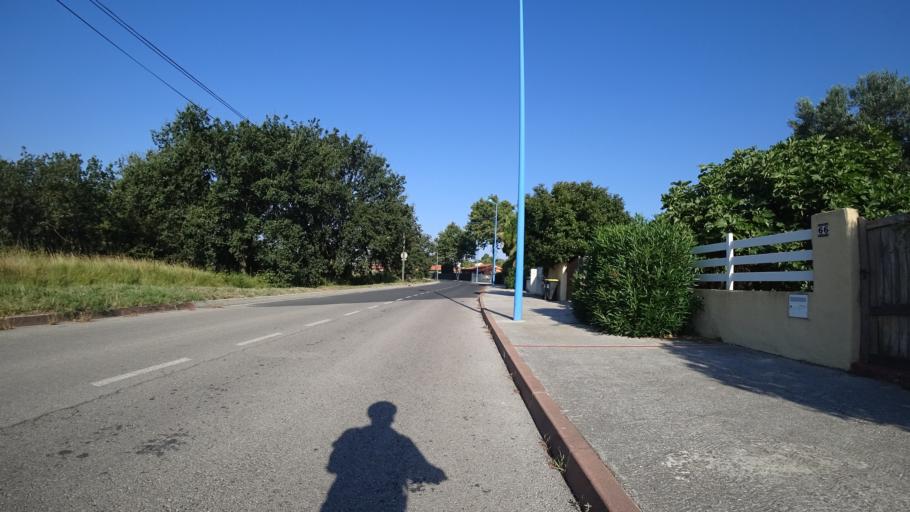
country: FR
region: Languedoc-Roussillon
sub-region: Departement des Pyrenees-Orientales
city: Canet-en-Roussillon
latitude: 42.6984
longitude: 2.9919
